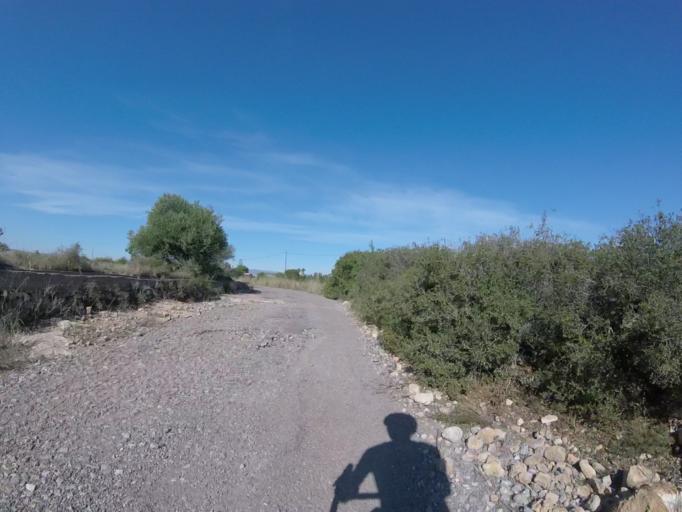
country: ES
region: Valencia
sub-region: Provincia de Castello
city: Torreblanca
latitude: 40.2085
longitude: 0.2406
